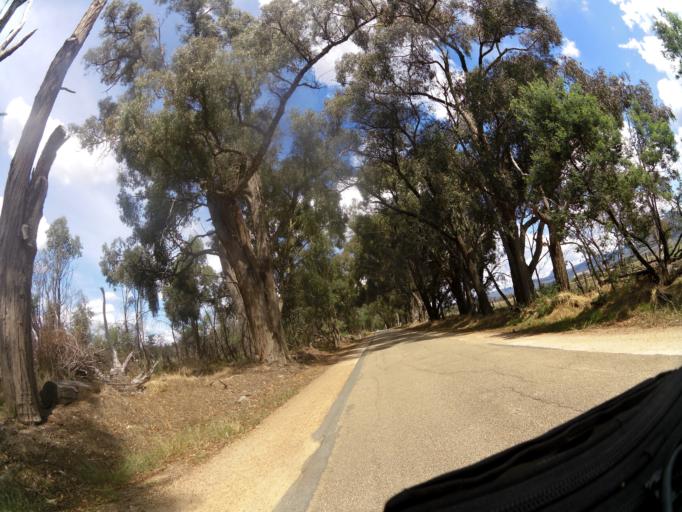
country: AU
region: Victoria
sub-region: Benalla
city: Benalla
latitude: -36.7690
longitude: 145.9754
